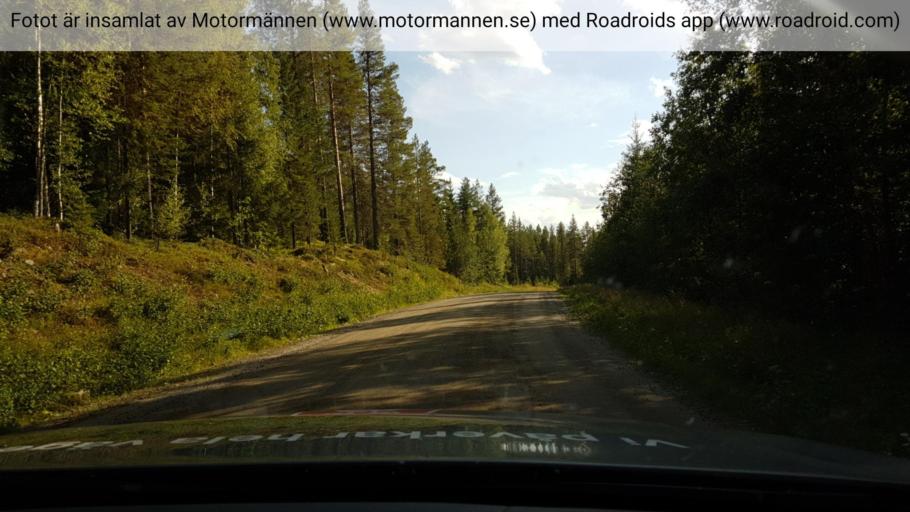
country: SE
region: Vaesternorrland
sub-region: Solleftea Kommun
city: As
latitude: 63.7429
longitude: 16.2538
